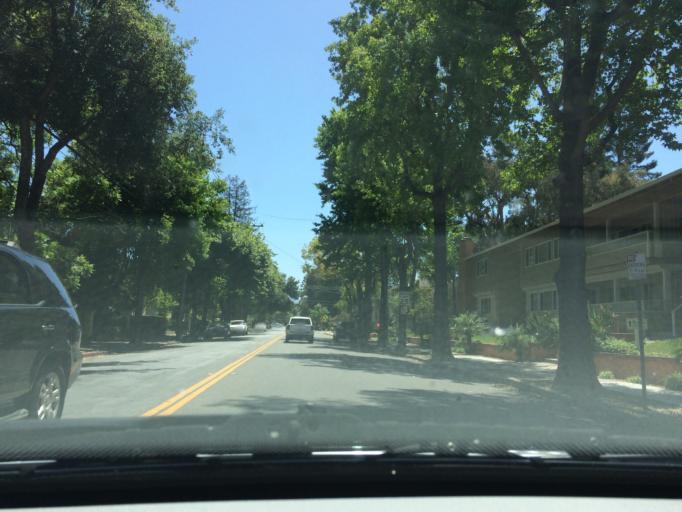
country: US
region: California
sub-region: San Mateo County
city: Menlo Park
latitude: 37.4572
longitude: -122.1821
